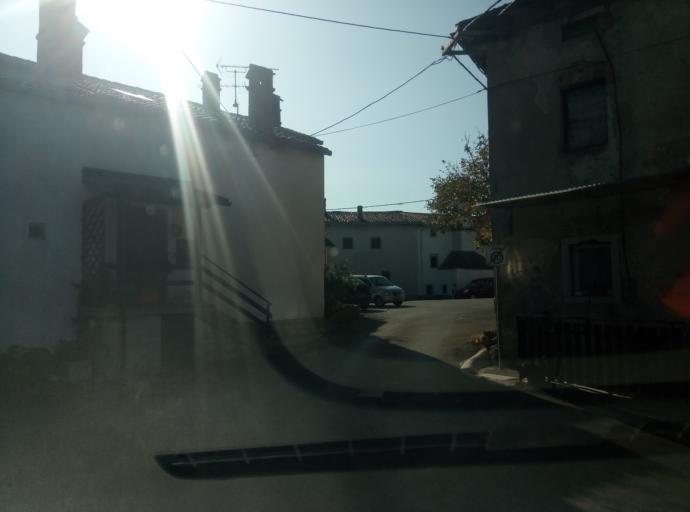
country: SI
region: Ajdovscina
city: Lokavec
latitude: 45.8164
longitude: 13.8521
